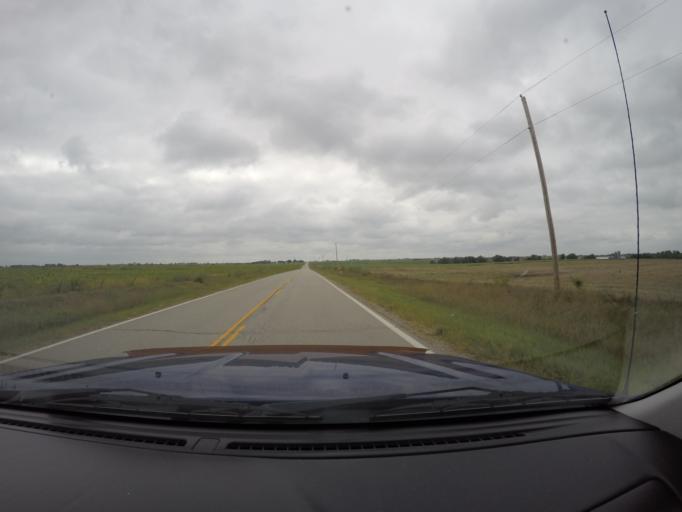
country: US
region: Kansas
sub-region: Morris County
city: Council Grove
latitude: 38.8407
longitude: -96.5148
